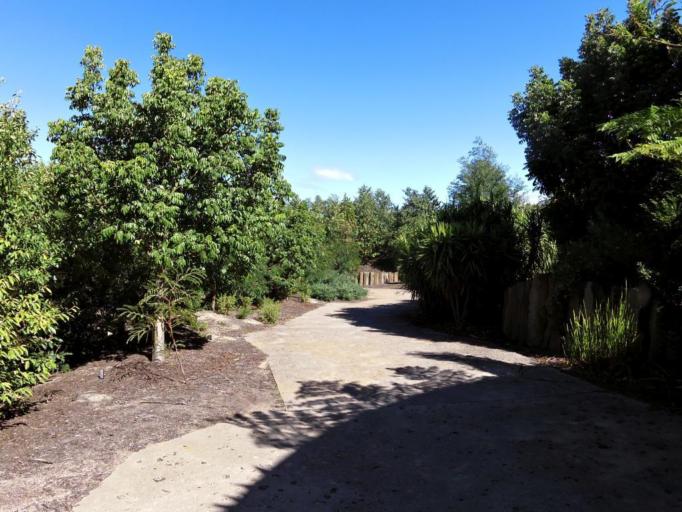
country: AU
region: Victoria
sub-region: Casey
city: Botanic Ridge
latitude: -38.1276
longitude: 145.2697
